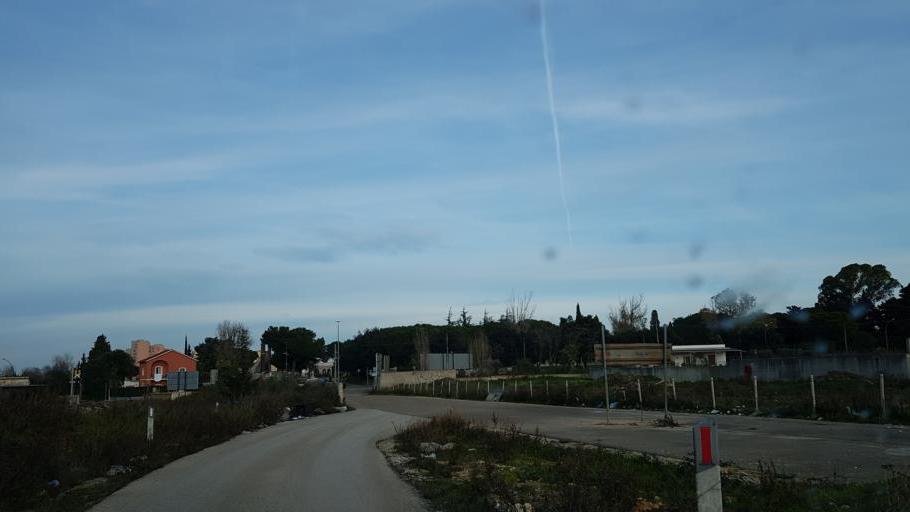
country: IT
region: Apulia
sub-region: Provincia di Brindisi
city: Brindisi
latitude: 40.6279
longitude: 17.9455
